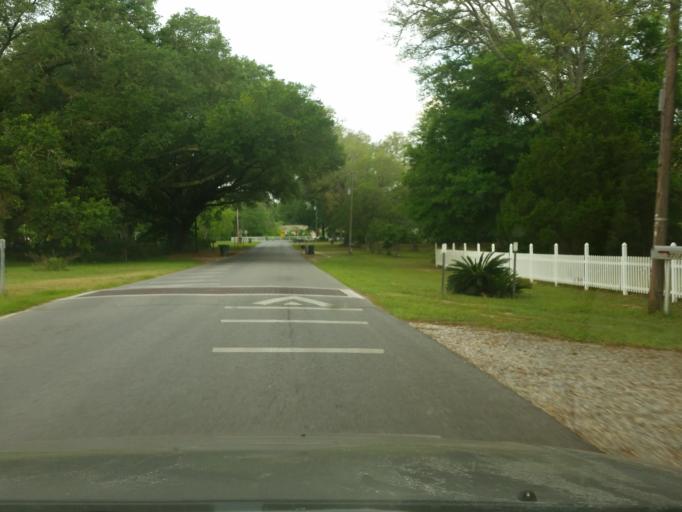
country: US
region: Florida
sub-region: Escambia County
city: Bellview
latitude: 30.4476
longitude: -87.3095
